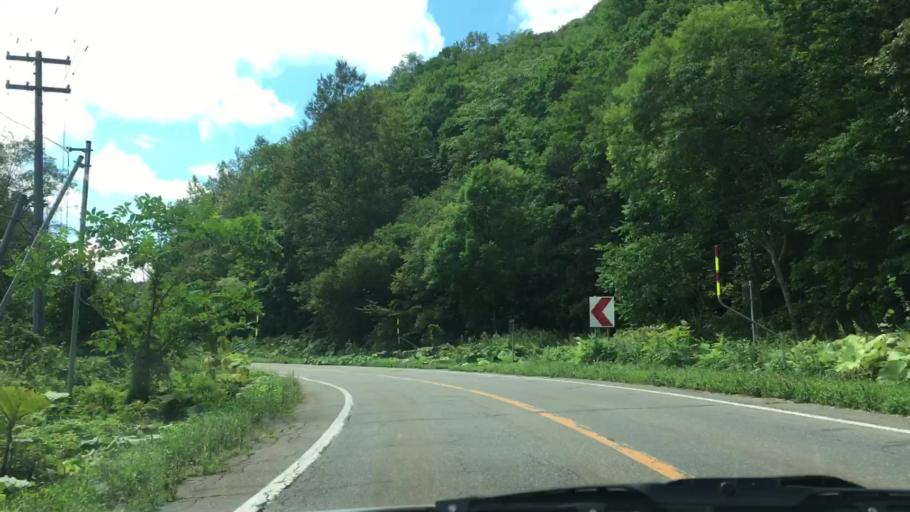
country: JP
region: Hokkaido
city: Kitami
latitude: 43.3503
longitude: 143.7775
